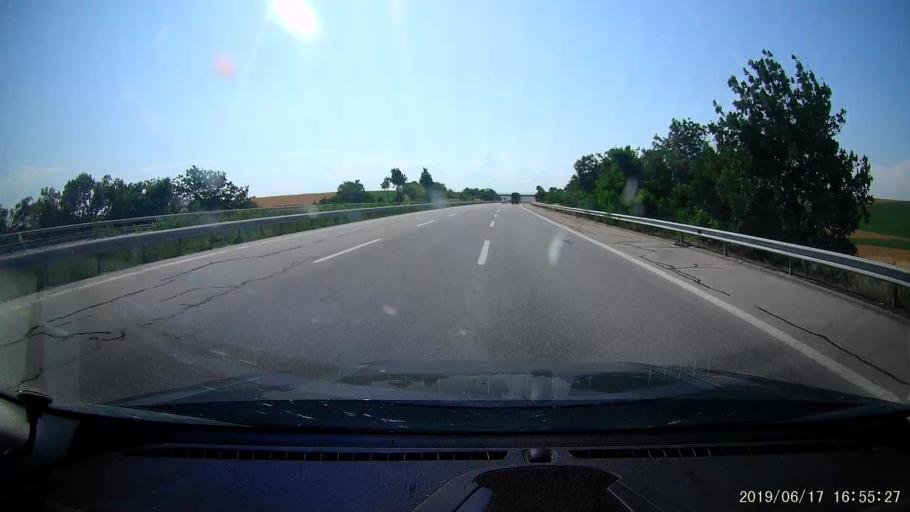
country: TR
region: Edirne
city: Haskoy
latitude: 41.5789
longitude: 26.9651
